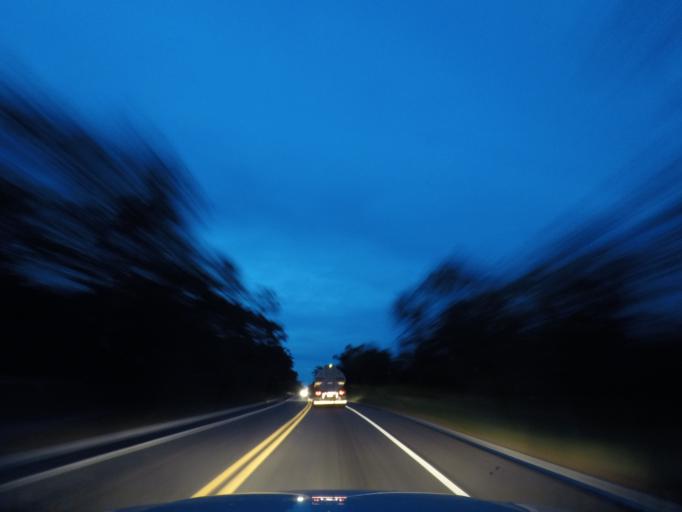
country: BR
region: Bahia
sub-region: Andarai
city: Vera Cruz
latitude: -12.4961
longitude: -41.3336
